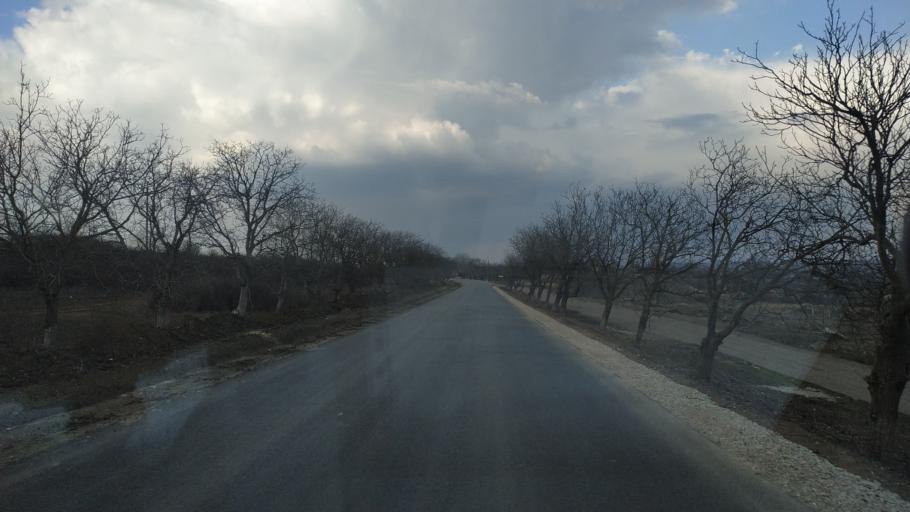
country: MD
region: Anenii Noi
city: Anenii Noi
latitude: 46.9988
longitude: 29.2868
